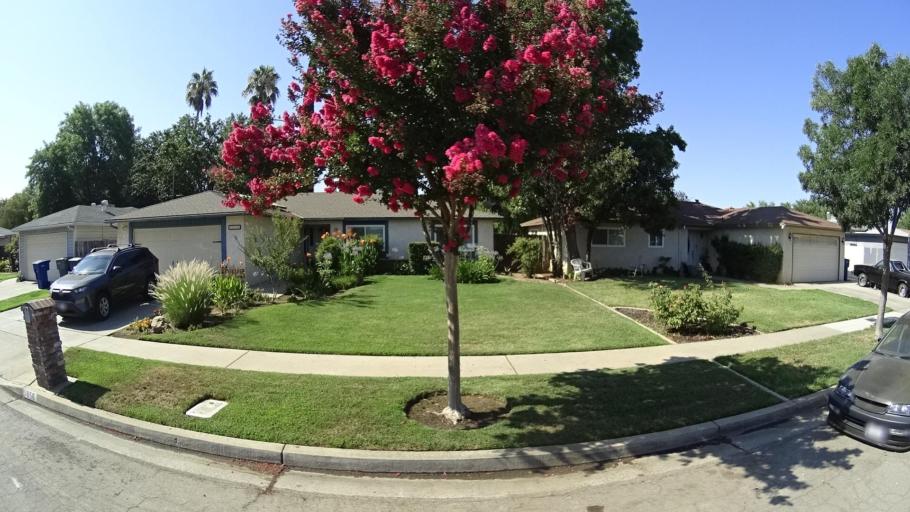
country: US
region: California
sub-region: Fresno County
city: Tarpey Village
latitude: 36.7883
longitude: -119.6885
